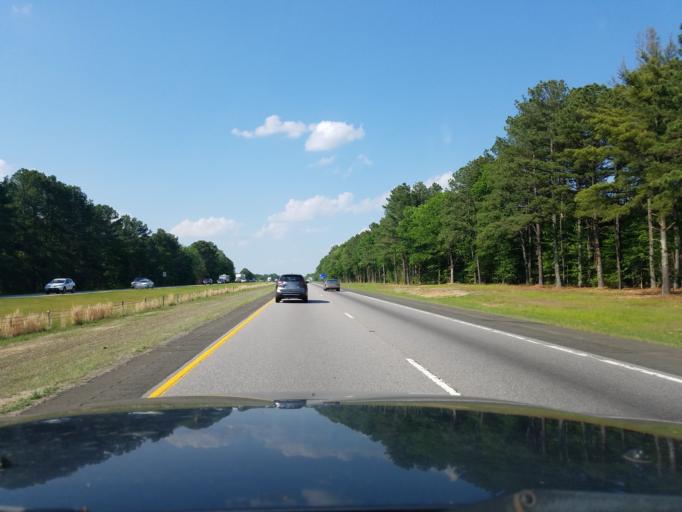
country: US
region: North Carolina
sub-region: Granville County
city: Butner
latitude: 36.1116
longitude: -78.7503
